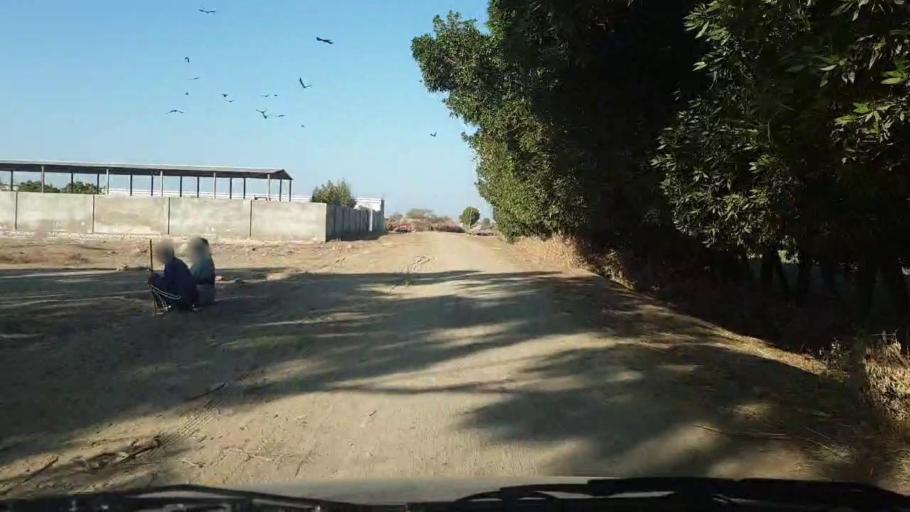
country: PK
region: Sindh
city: Samaro
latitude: 25.3614
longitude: 69.3021
